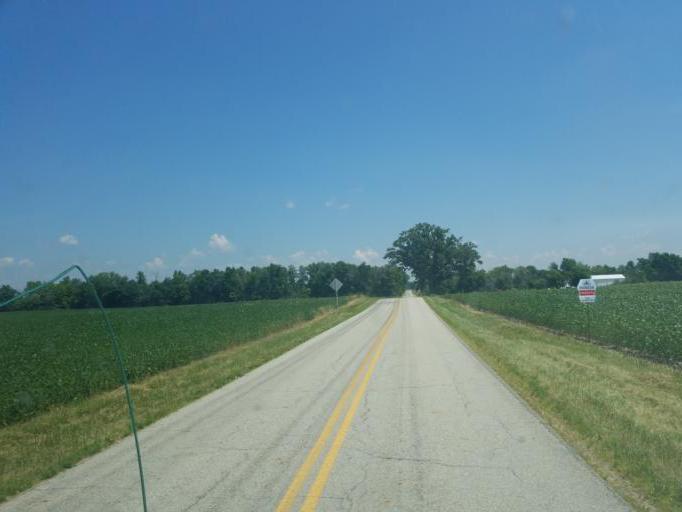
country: US
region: Ohio
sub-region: Shelby County
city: Botkins
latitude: 40.4821
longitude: -84.2297
